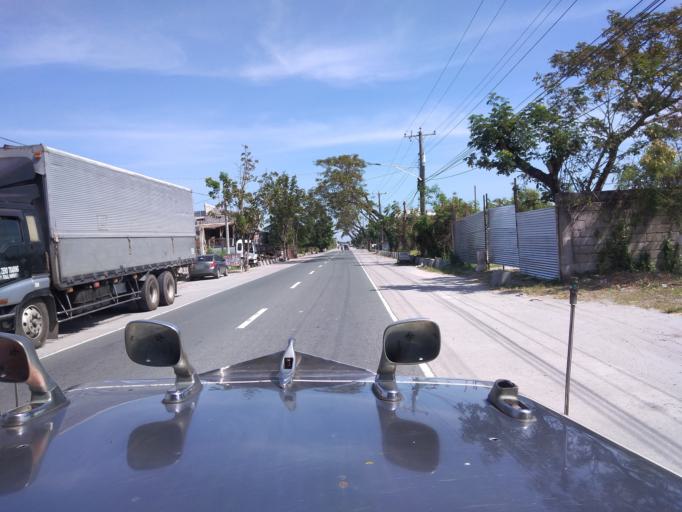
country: PH
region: Central Luzon
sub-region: Province of Pampanga
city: San Juan
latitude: 15.0128
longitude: 120.6639
